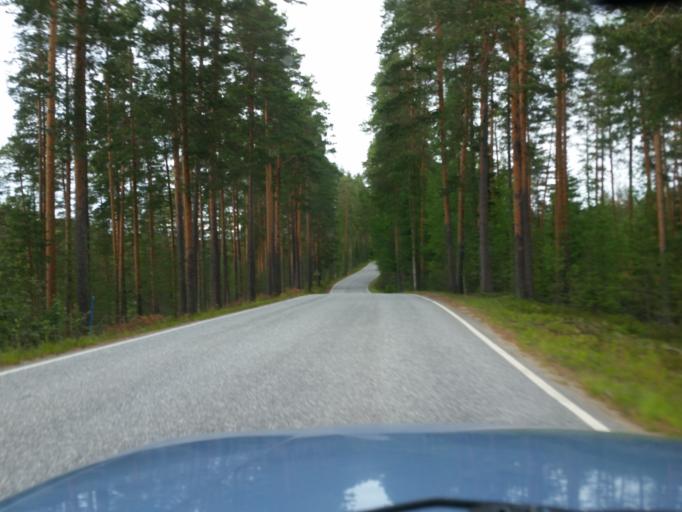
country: FI
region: Southern Savonia
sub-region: Savonlinna
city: Sulkava
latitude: 61.7814
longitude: 28.4252
